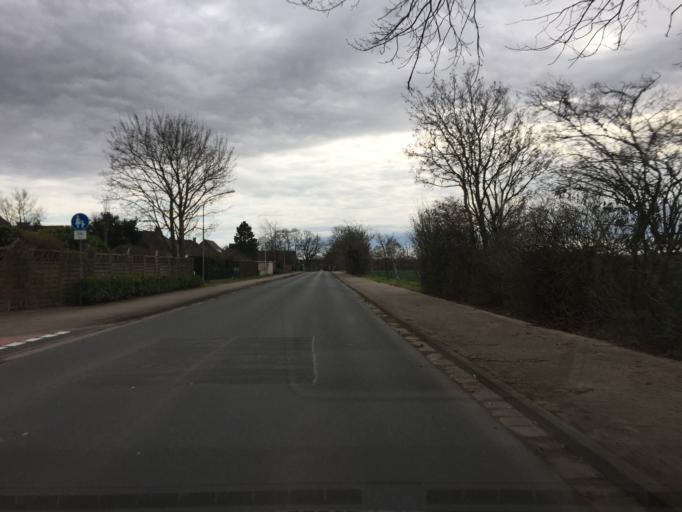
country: DE
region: Lower Saxony
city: Garbsen
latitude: 52.4386
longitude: 9.5734
